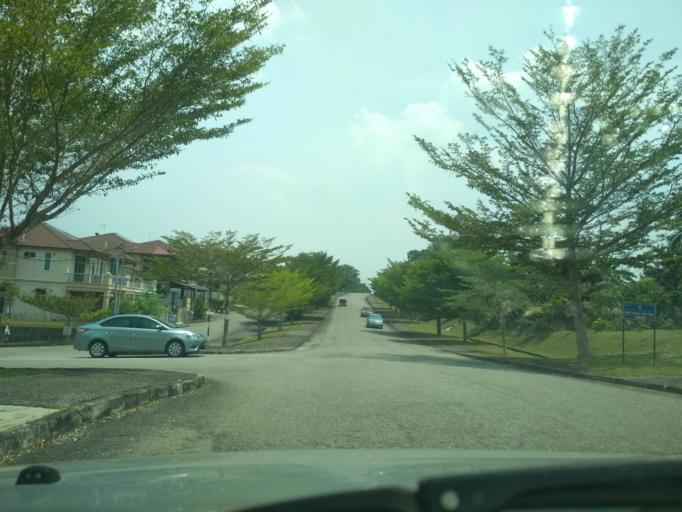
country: MY
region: Kedah
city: Kulim
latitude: 5.3616
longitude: 100.5332
